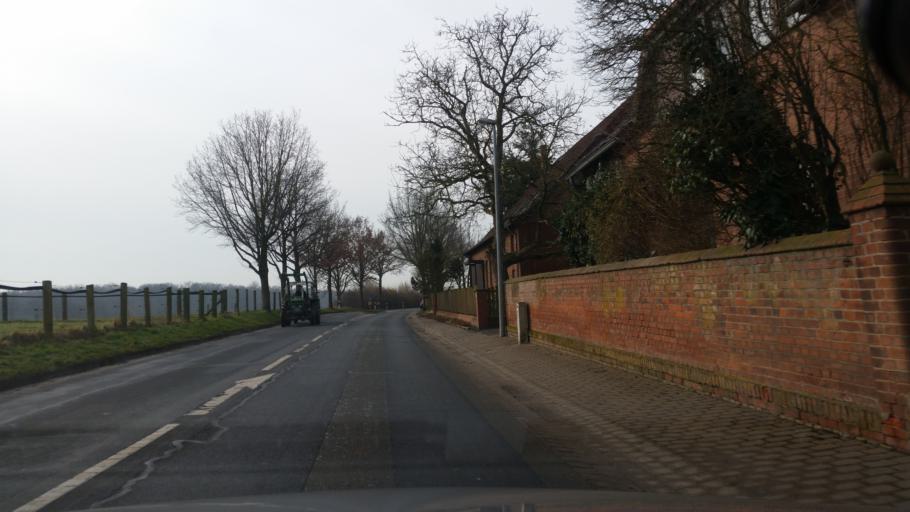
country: DE
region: Lower Saxony
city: Seelze
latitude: 52.3721
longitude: 9.5882
